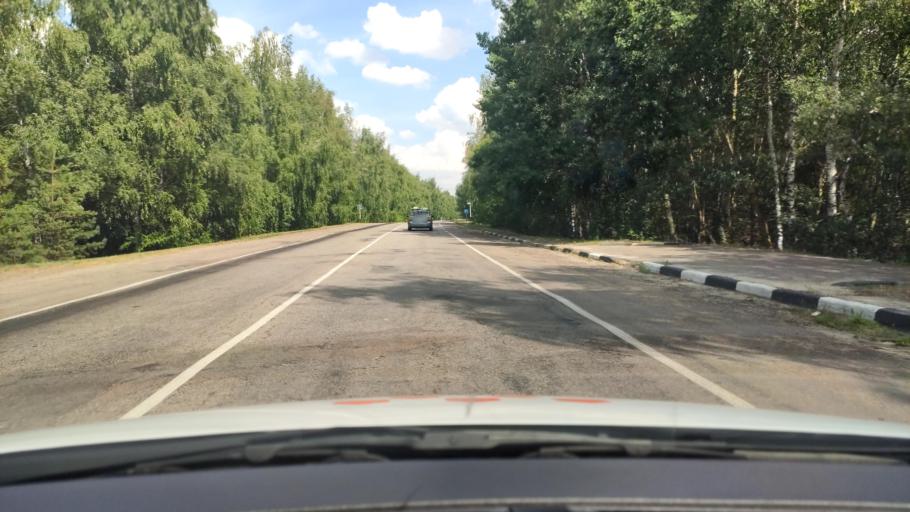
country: RU
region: Voronezj
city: Sadovoye
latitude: 51.7808
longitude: 40.5420
